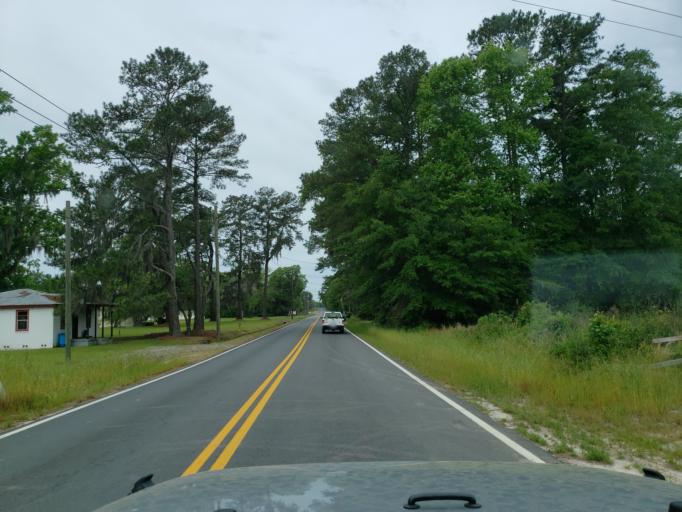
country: US
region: Georgia
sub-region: Chatham County
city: Port Wentworth
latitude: 32.1800
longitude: -81.1955
